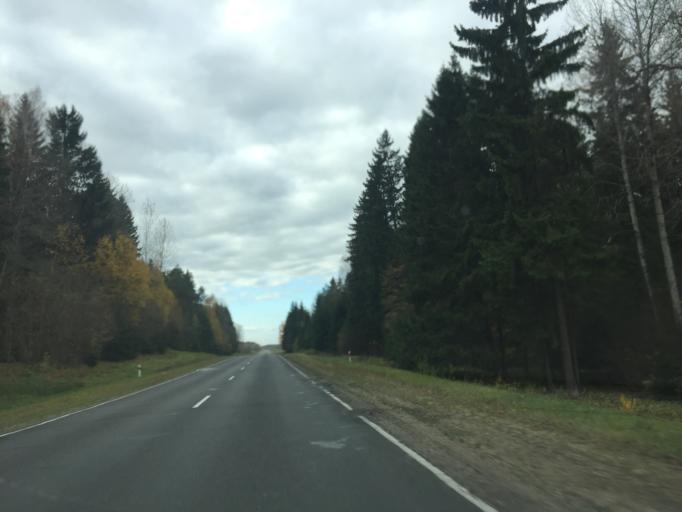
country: BY
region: Vitebsk
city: Mosar
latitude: 55.0663
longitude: 27.3218
